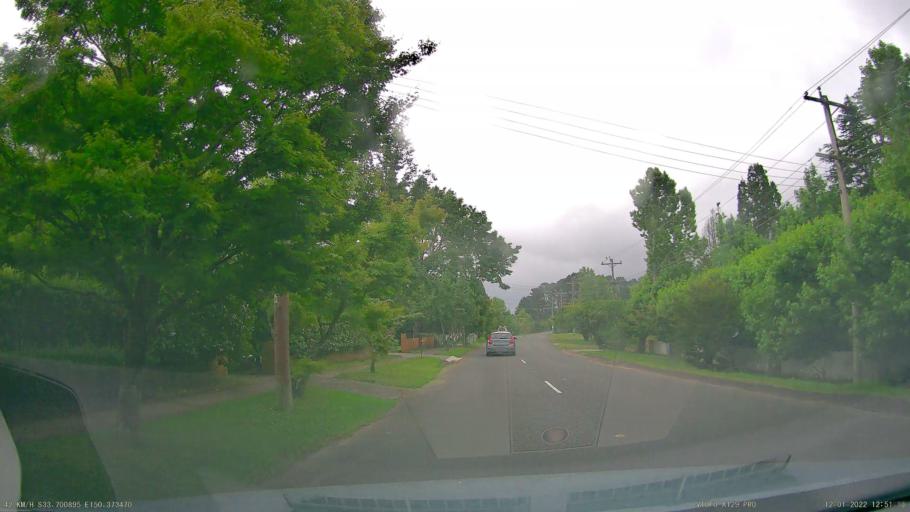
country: AU
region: New South Wales
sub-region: Blue Mountains Municipality
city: Leura
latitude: -33.7007
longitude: 150.3734
